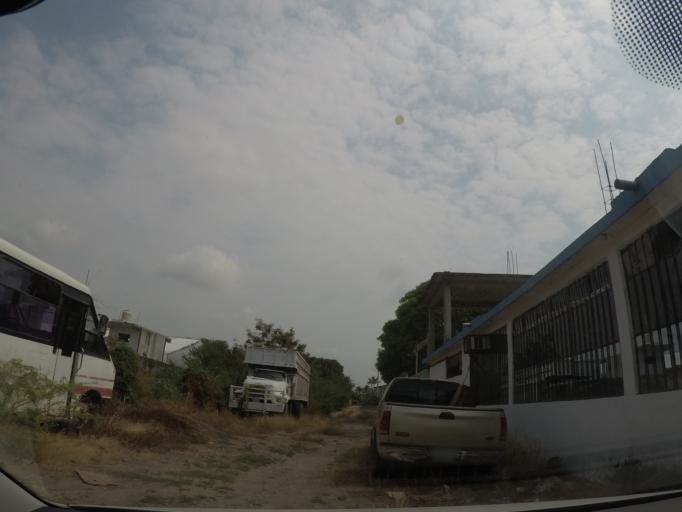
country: MX
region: Oaxaca
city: Juchitan de Zaragoza
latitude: 16.4466
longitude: -95.0267
